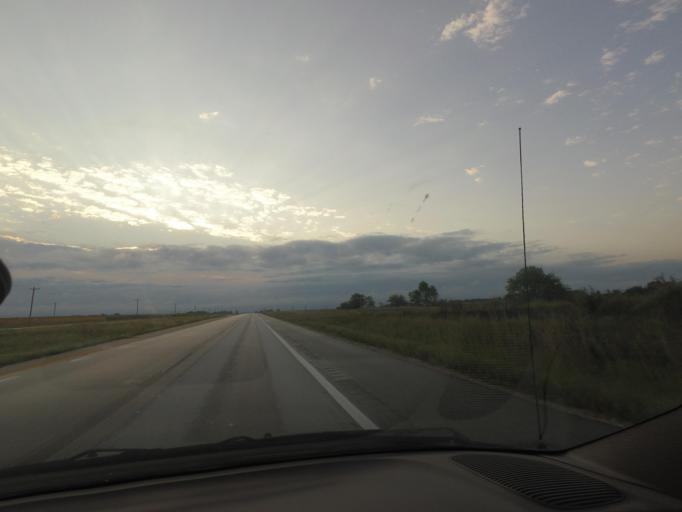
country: US
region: Missouri
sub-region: Shelby County
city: Shelbina
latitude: 39.7149
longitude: -92.1309
